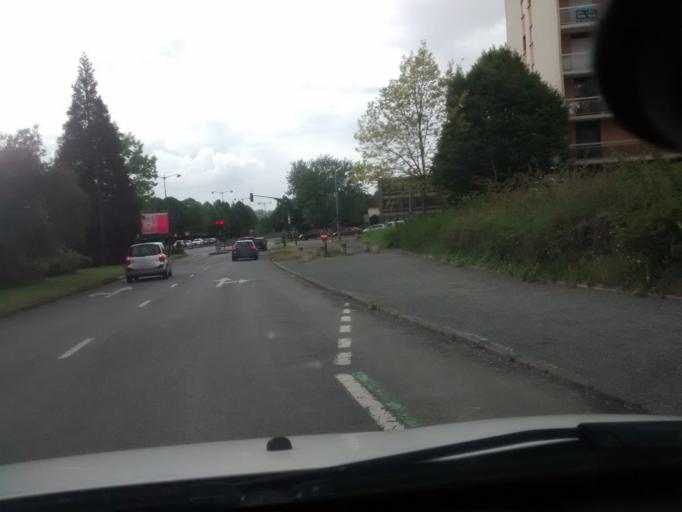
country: FR
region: Brittany
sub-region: Departement d'Ille-et-Vilaine
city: Rennes
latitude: 48.1284
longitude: -1.6628
